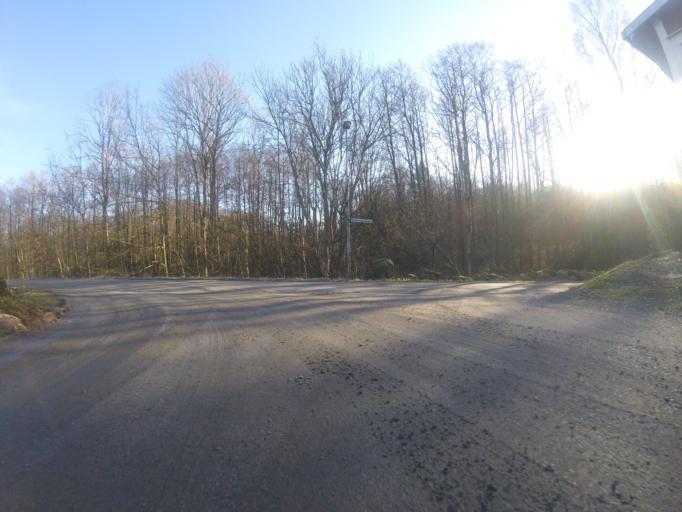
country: SE
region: Halland
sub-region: Varbergs Kommun
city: Veddige
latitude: 57.2314
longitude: 12.3106
